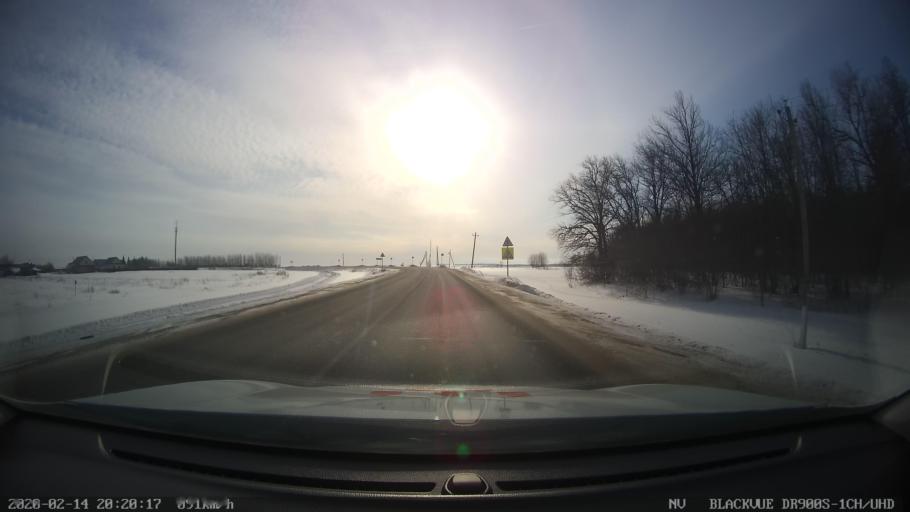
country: RU
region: Tatarstan
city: Verkhniy Uslon
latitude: 55.5585
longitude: 48.9041
